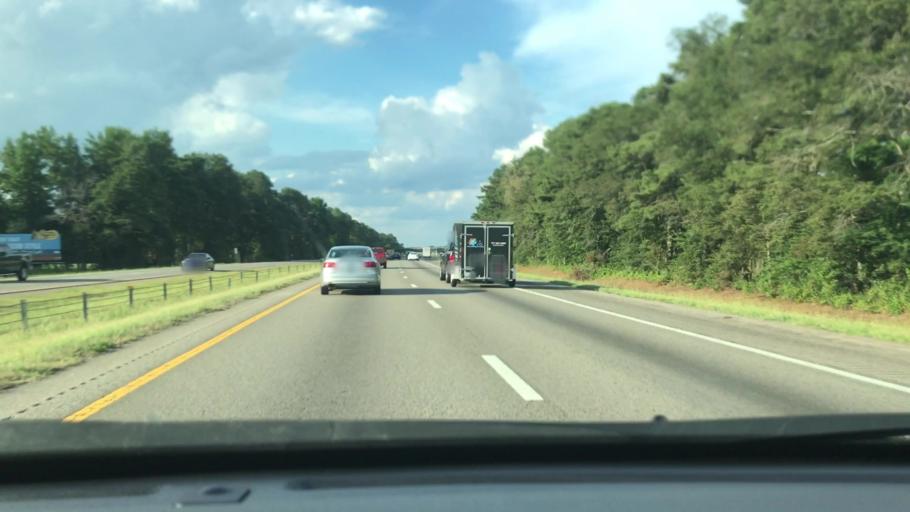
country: US
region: North Carolina
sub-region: Cumberland County
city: Hope Mills
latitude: 34.9152
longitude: -78.9521
